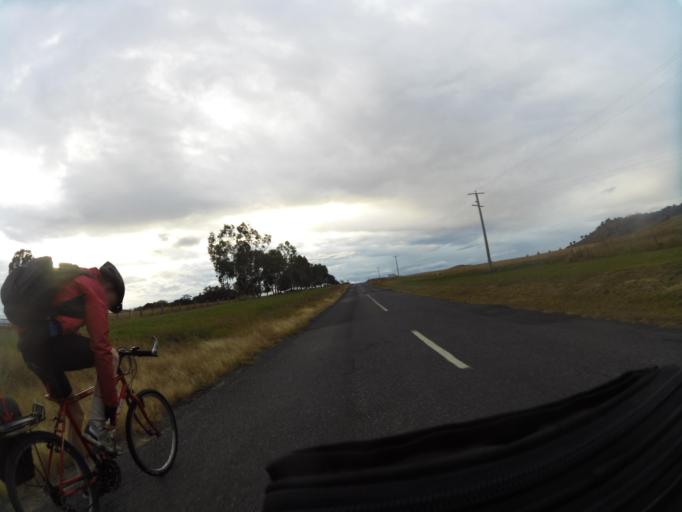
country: AU
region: New South Wales
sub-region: Greater Hume Shire
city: Holbrook
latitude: -36.0503
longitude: 147.9321
